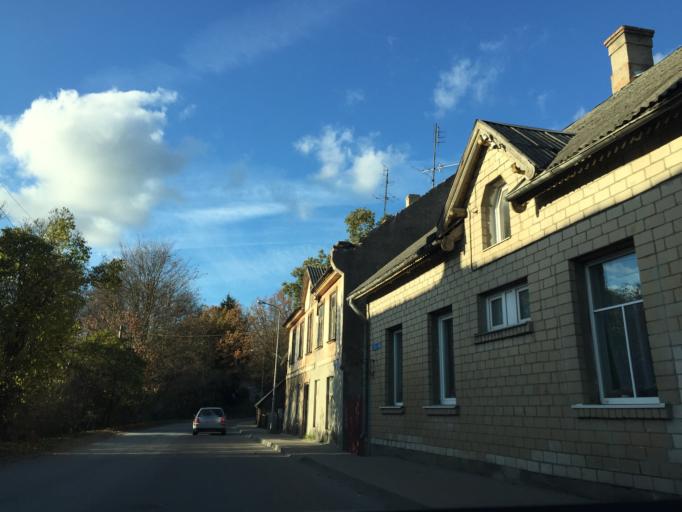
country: LV
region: Tukuma Rajons
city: Tukums
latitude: 56.9689
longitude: 23.1403
